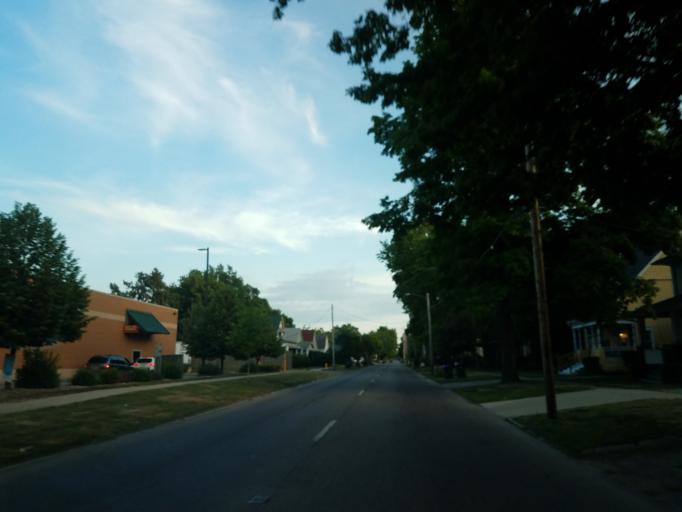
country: US
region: Illinois
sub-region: McLean County
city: Bloomington
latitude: 40.4711
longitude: -88.9942
